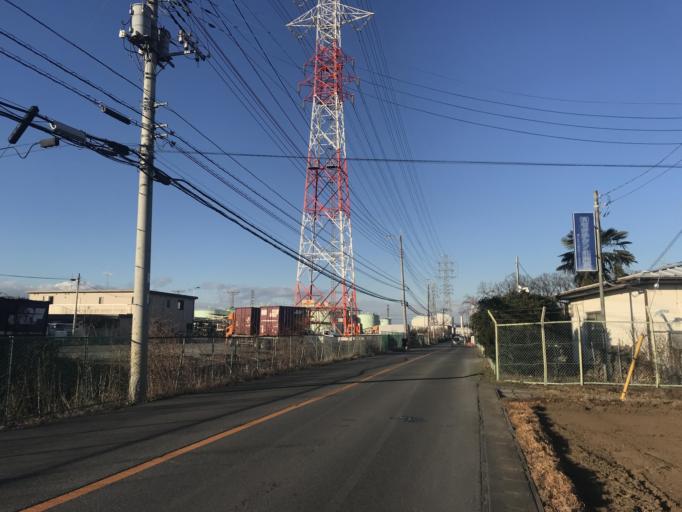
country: JP
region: Tochigi
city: Kaminokawa
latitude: 36.4445
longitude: 139.8711
